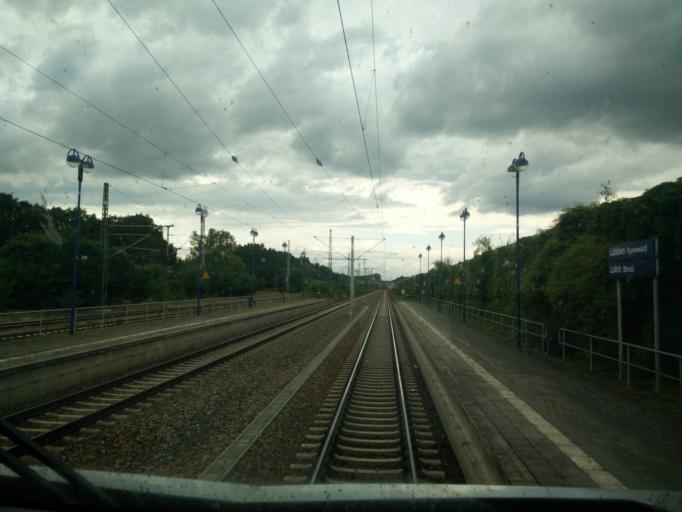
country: DE
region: Brandenburg
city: Luebben
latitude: 51.9405
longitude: 13.8760
